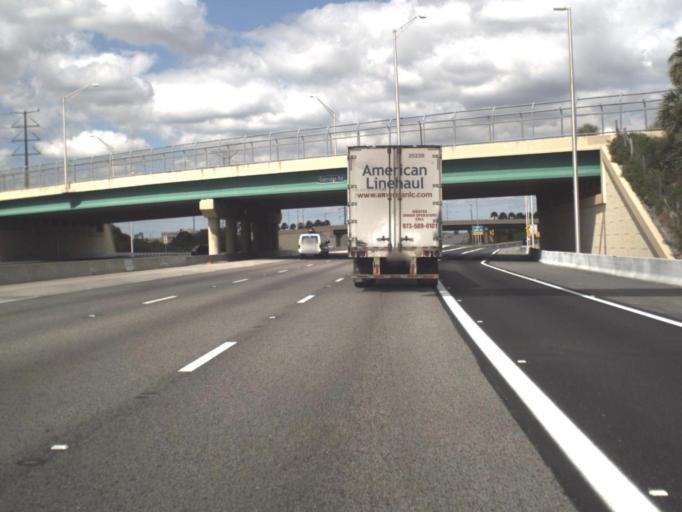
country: US
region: Florida
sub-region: Orange County
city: Tangelo Park
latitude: 28.4714
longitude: -81.4436
